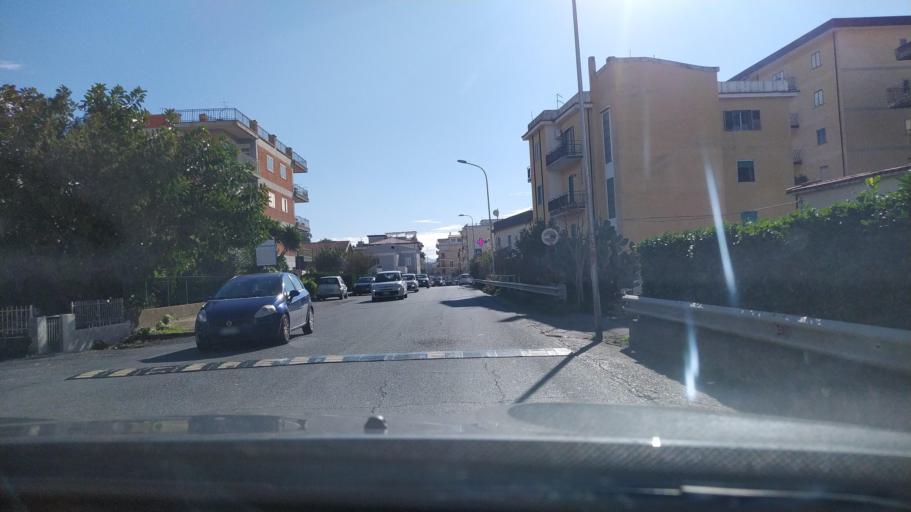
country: IT
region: Calabria
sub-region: Provincia di Cosenza
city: Paola
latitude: 39.3693
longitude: 16.0284
